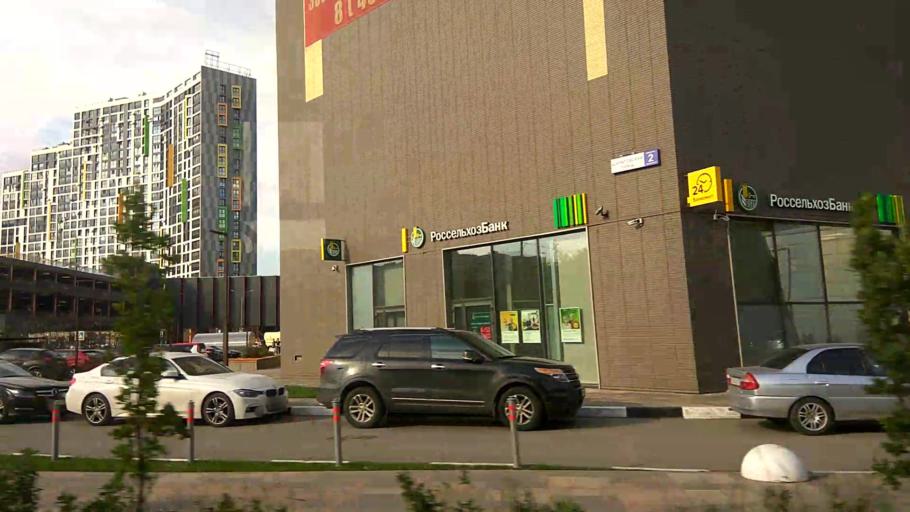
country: RU
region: Moskovskaya
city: Mytishchi
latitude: 55.9157
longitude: 37.7558
